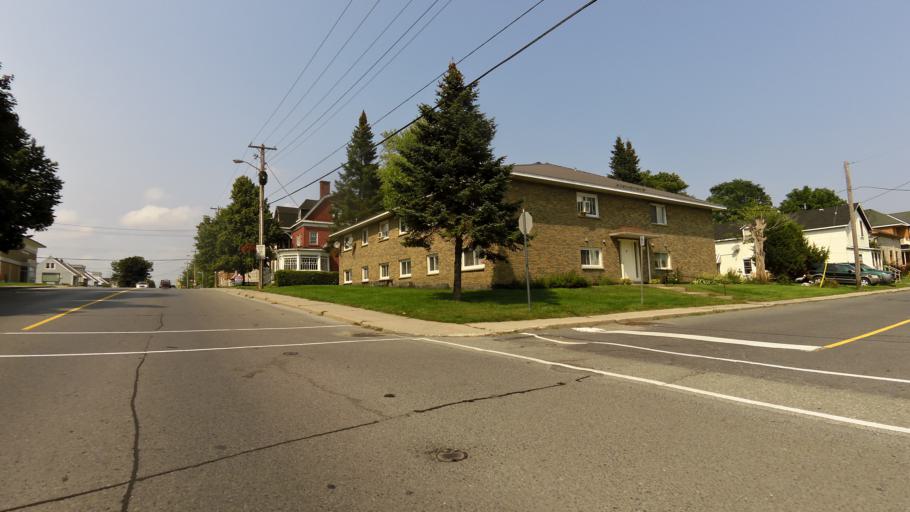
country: CA
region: Ontario
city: Prescott
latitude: 44.7117
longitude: -75.5144
